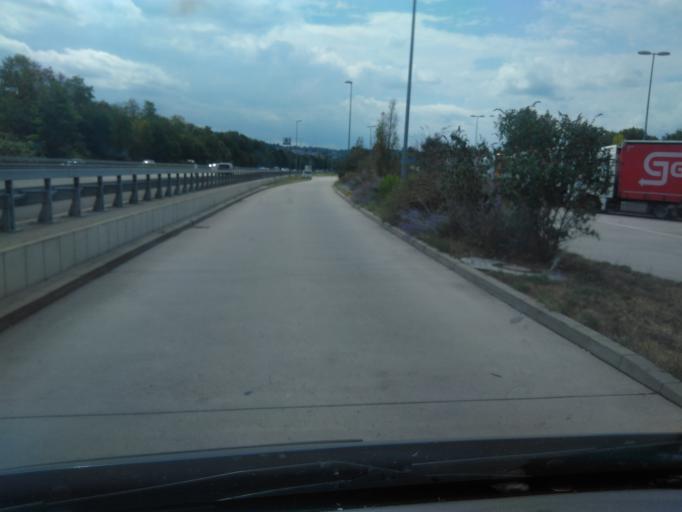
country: DE
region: Baden-Wuerttemberg
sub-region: Freiburg Region
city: Bad Bellingen
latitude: 47.7398
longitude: 7.5522
